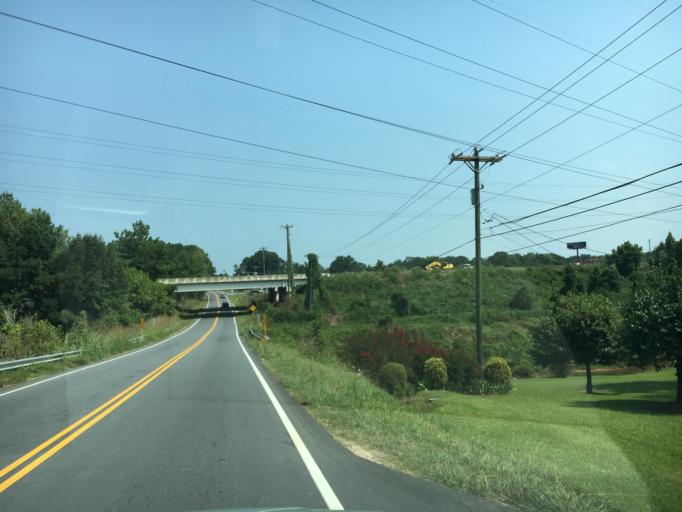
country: US
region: South Carolina
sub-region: Spartanburg County
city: Valley Falls
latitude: 35.0113
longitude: -81.9501
